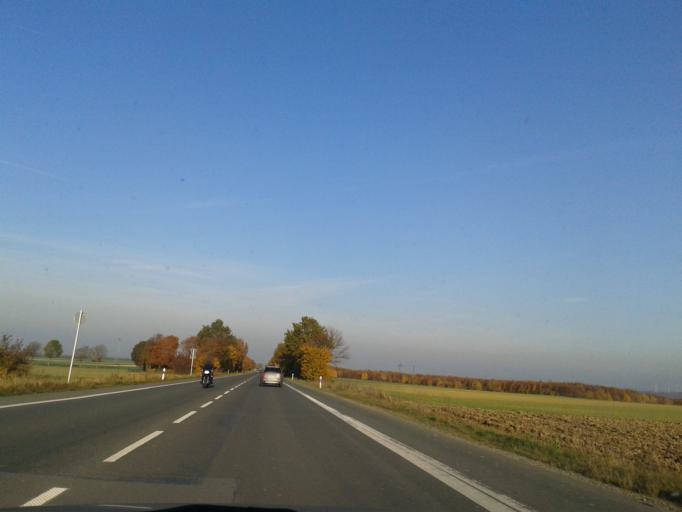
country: DE
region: North Rhine-Westphalia
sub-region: Regierungsbezirk Detmold
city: Buren
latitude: 51.5705
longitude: 8.5438
